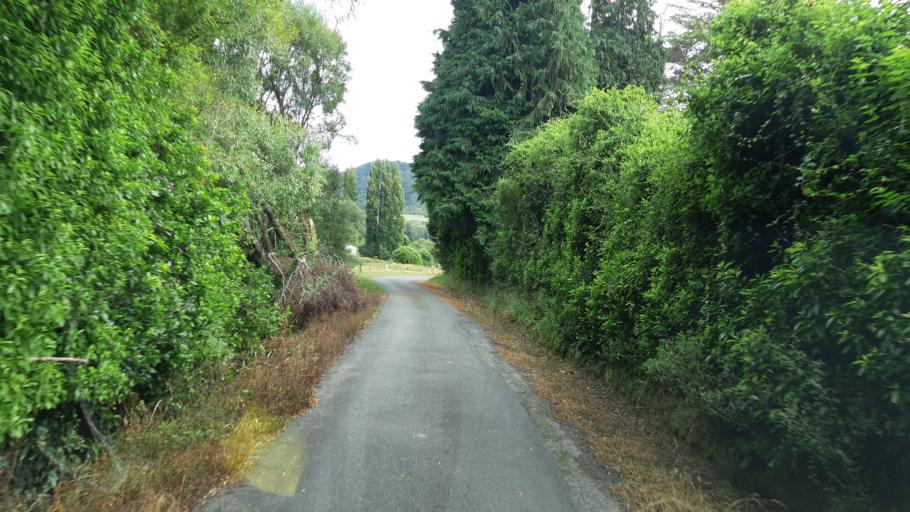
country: NZ
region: West Coast
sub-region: Buller District
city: Westport
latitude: -41.7821
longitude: 172.2754
